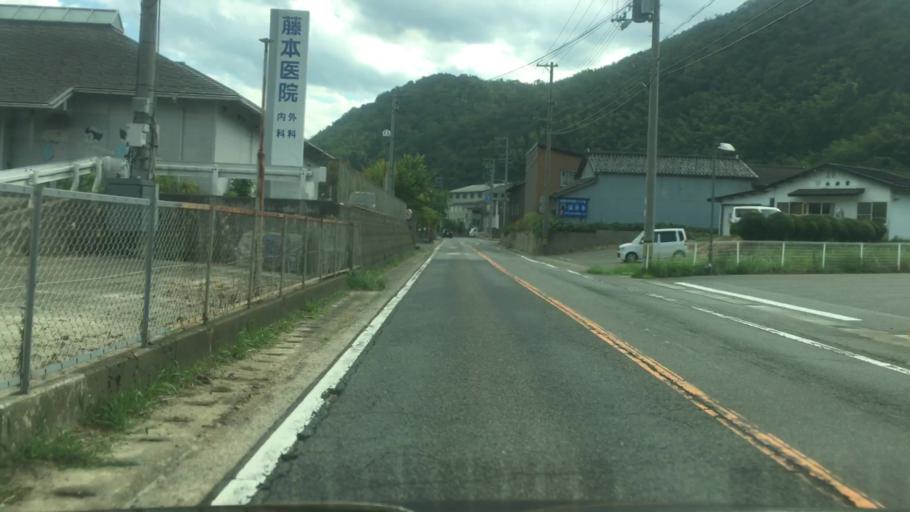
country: JP
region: Hyogo
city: Toyooka
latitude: 35.6054
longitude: 134.8025
